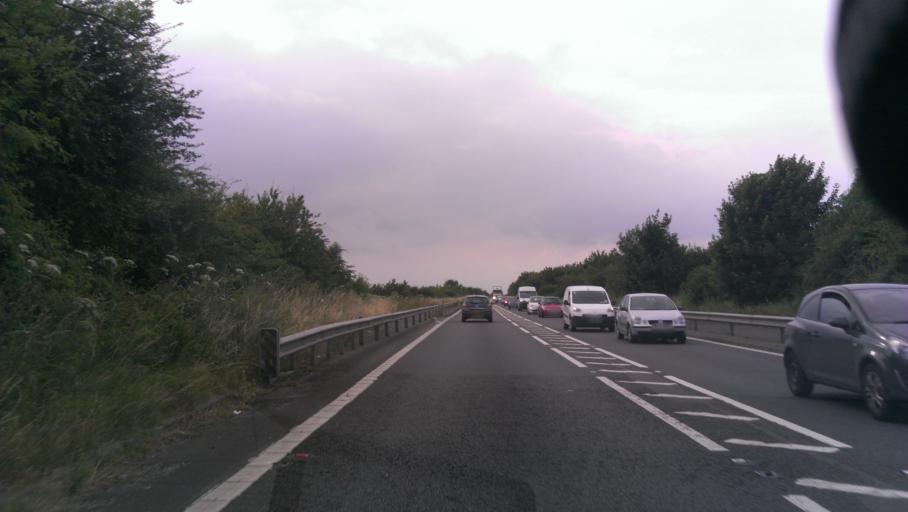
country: GB
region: England
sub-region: Kent
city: Dover
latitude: 51.1587
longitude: 1.2752
